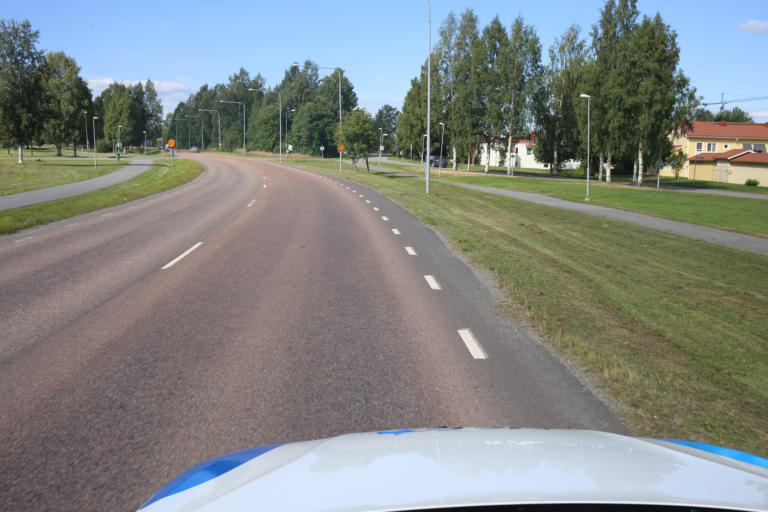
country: SE
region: Vaesterbotten
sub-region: Skelleftea Kommun
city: Skelleftea
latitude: 64.7452
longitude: 20.9757
